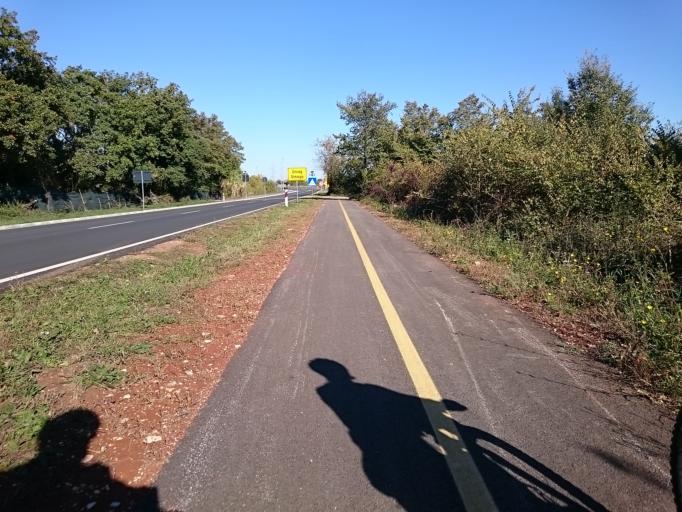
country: HR
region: Istarska
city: Umag
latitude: 45.4186
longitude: 13.5305
